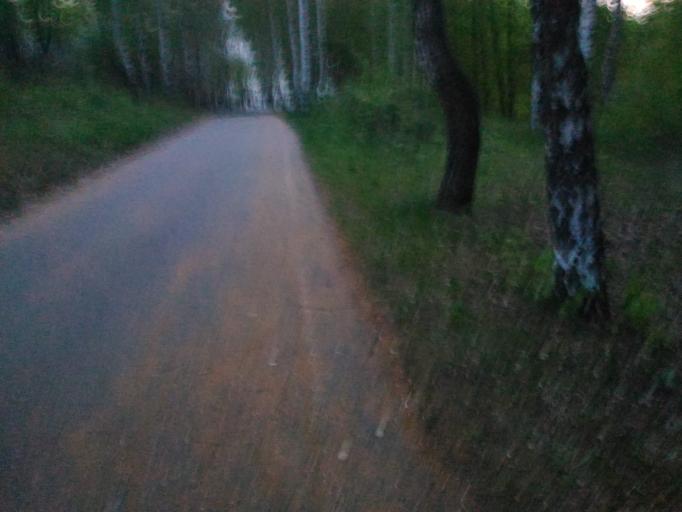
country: RU
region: Ulyanovsk
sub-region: Ulyanovskiy Rayon
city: Ulyanovsk
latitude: 54.2752
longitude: 48.3543
